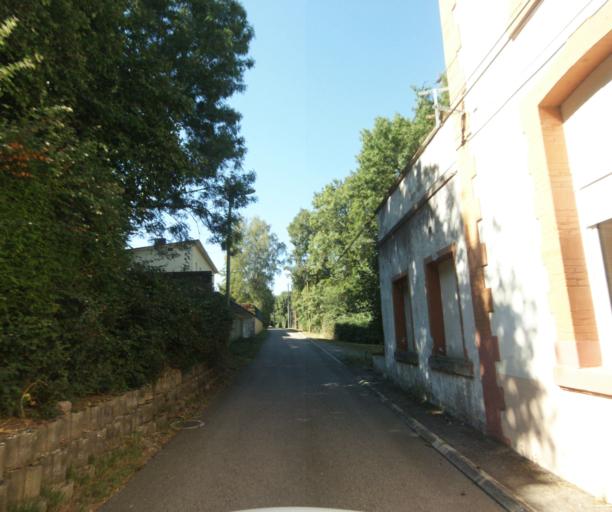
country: FR
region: Lorraine
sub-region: Departement des Vosges
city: Chantraine
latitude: 48.1582
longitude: 6.4571
